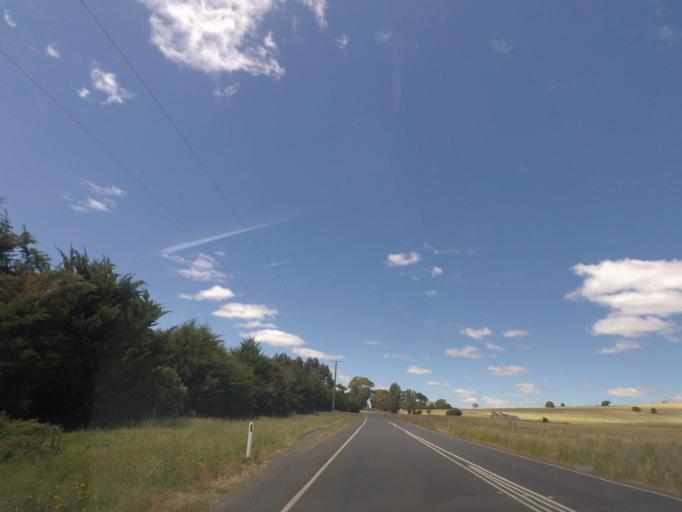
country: AU
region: Victoria
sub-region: Mount Alexander
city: Castlemaine
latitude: -37.3231
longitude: 144.1955
